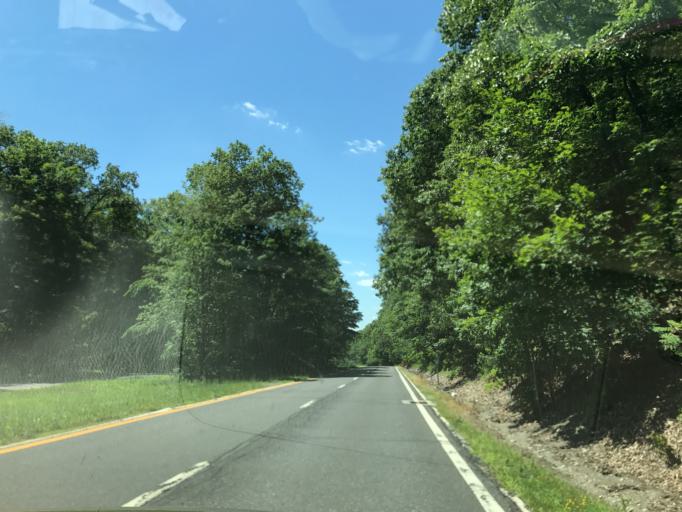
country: US
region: New York
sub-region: Dutchess County
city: Hillside Lake
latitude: 41.6820
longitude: -73.7869
